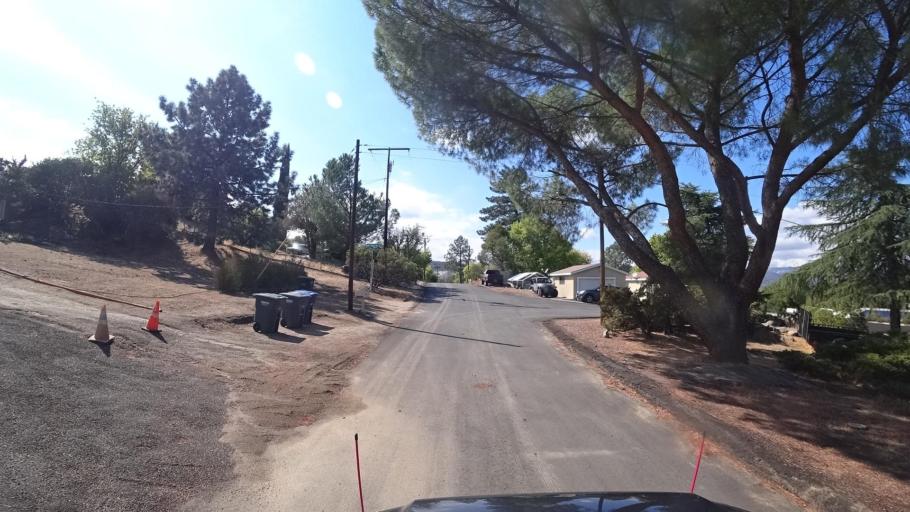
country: US
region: California
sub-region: San Diego County
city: Campo
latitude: 32.6779
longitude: -116.5010
